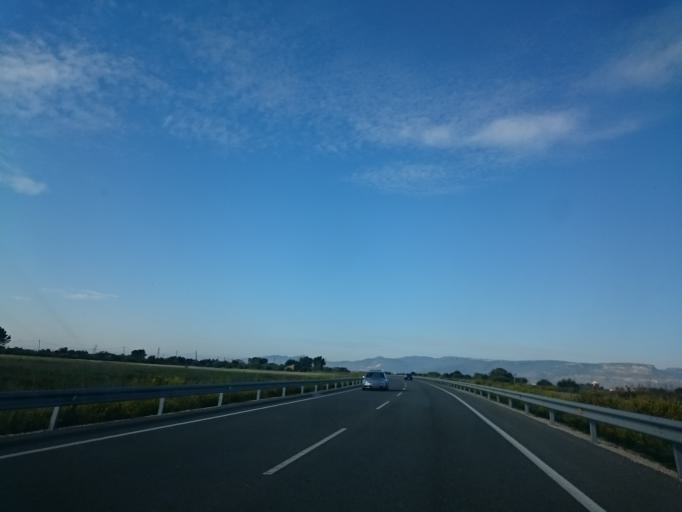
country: ES
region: Catalonia
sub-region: Provincia de Tarragona
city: Puigpelat
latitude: 41.2925
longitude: 1.2822
